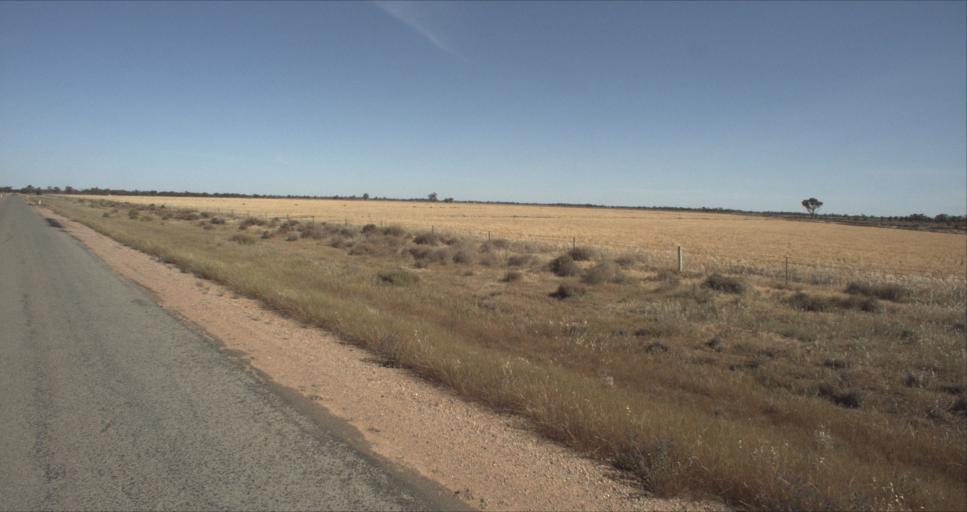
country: AU
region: New South Wales
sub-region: Leeton
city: Leeton
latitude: -34.4905
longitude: 146.3827
